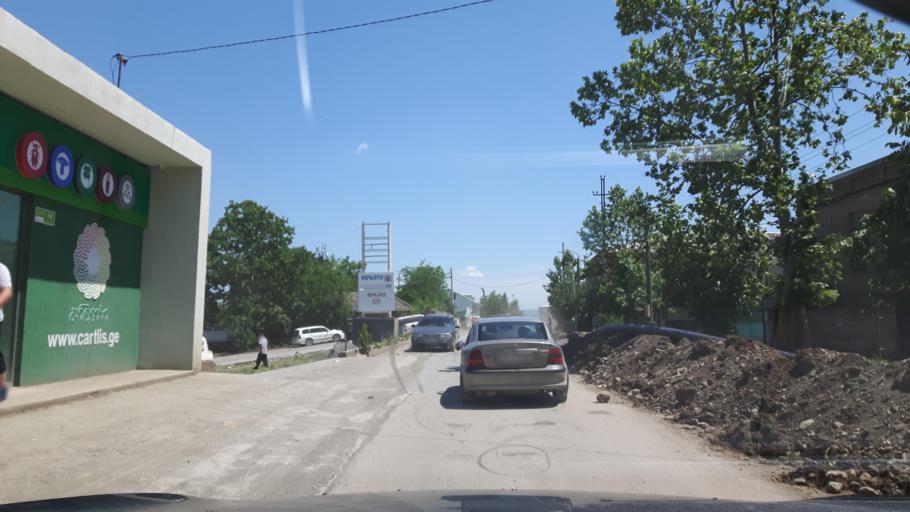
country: GE
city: Tsnori
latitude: 41.6195
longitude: 45.9820
